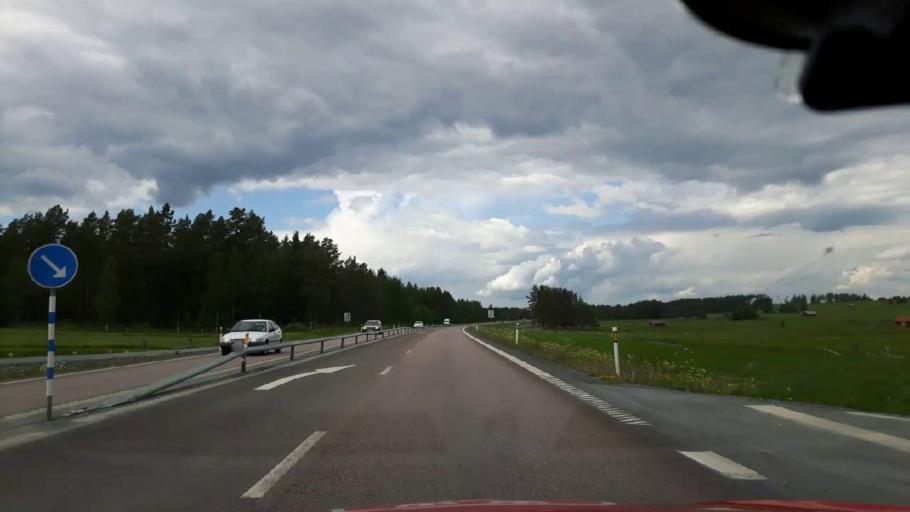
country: SE
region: Jaemtland
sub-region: OEstersunds Kommun
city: Ostersund
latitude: 63.2555
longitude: 14.5645
